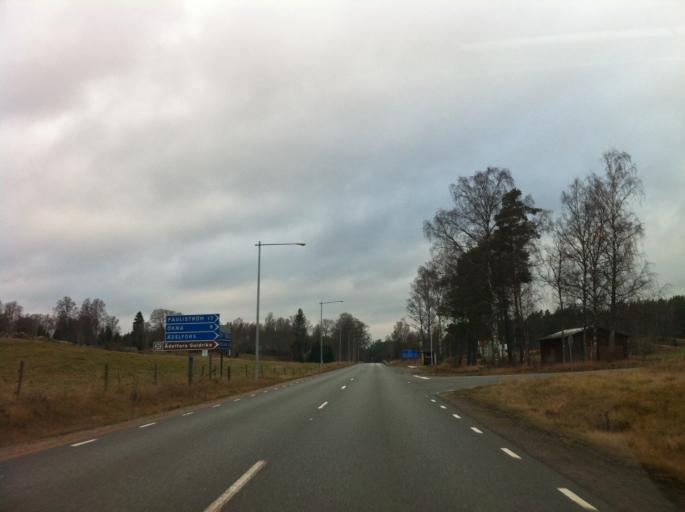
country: SE
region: Kronoberg
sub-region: Uppvidinge Kommun
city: Aseda
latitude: 57.4025
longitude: 15.3183
